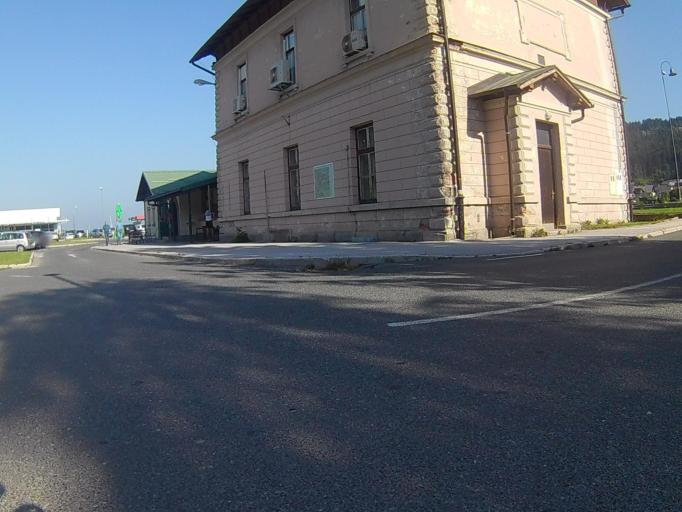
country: SI
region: Mislinja
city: Mislinja
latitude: 46.4426
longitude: 15.1929
